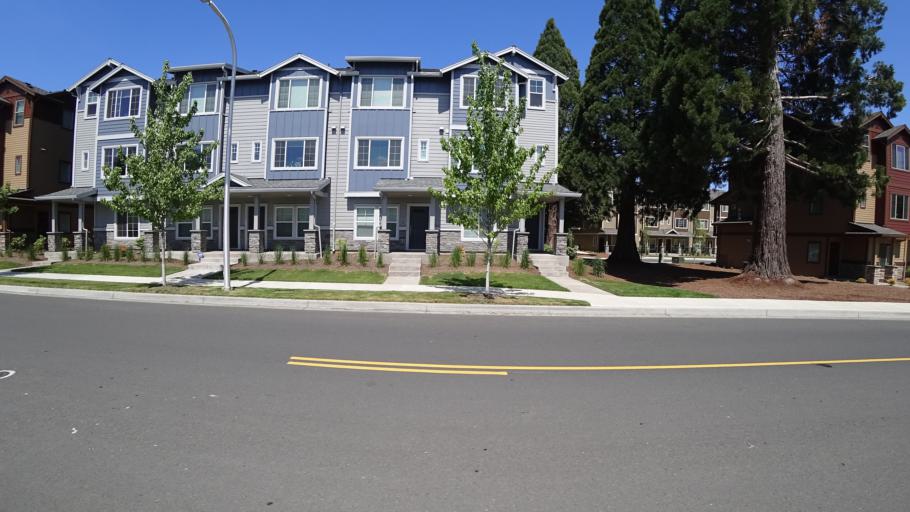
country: US
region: Oregon
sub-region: Washington County
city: Aloha
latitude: 45.5166
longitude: -122.8980
